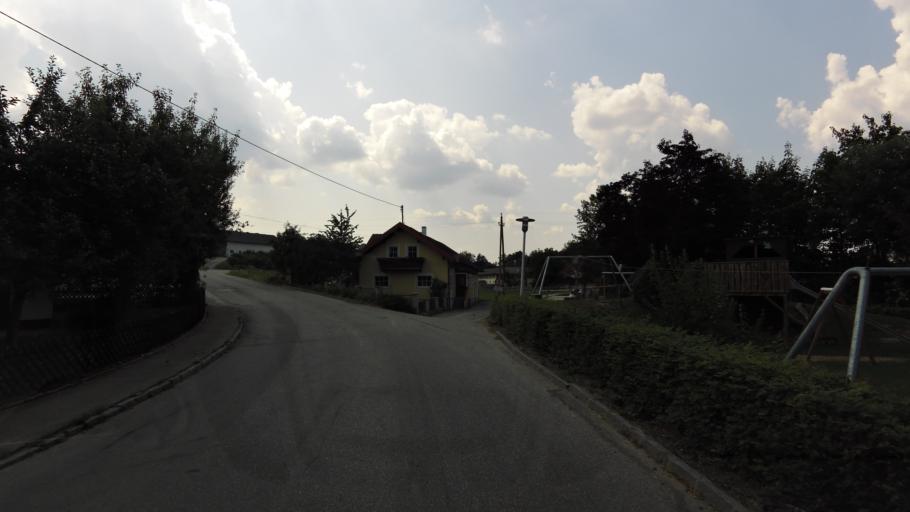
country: AT
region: Upper Austria
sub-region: Politischer Bezirk Ried im Innkreis
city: Waldzell
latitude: 48.1340
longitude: 13.4267
